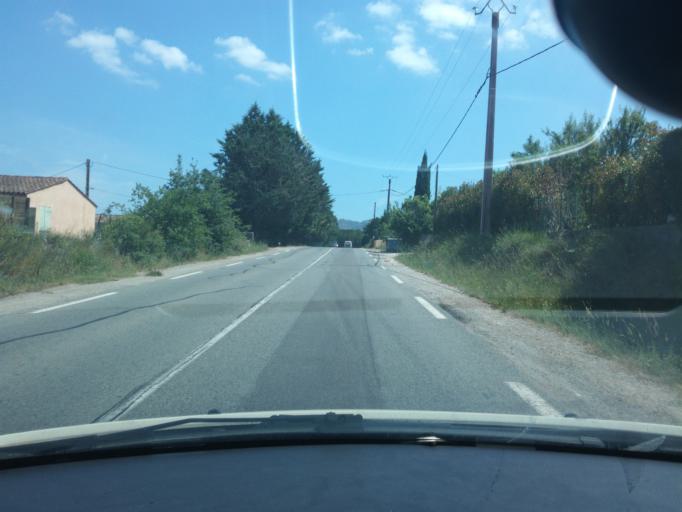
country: FR
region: Provence-Alpes-Cote d'Azur
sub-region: Departement du Var
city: Le Muy
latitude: 43.4879
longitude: 6.5657
